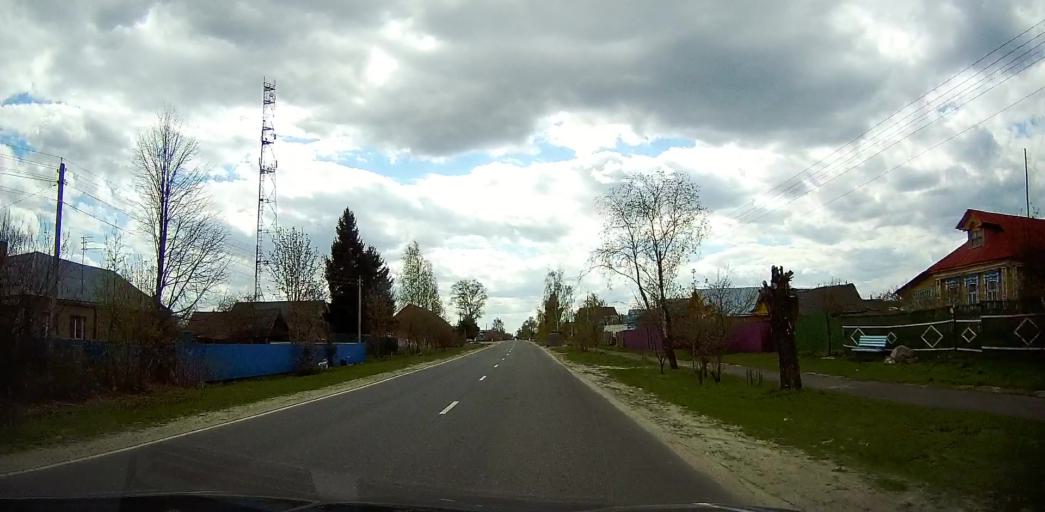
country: RU
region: Moskovskaya
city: Drezna
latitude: 55.6697
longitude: 38.7653
